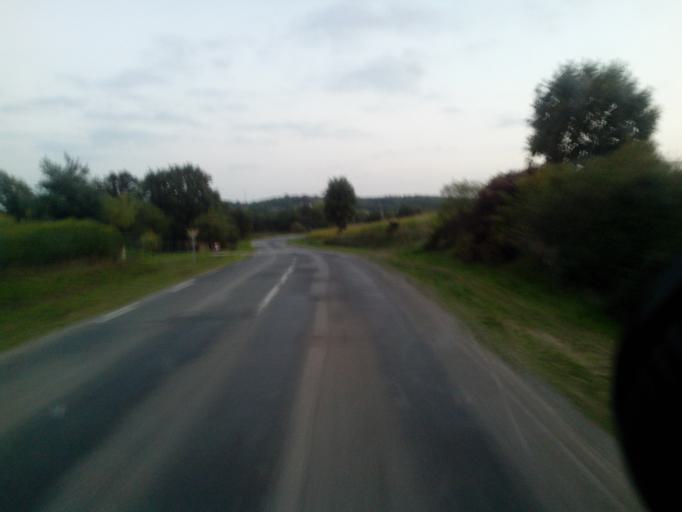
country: FR
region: Brittany
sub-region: Departement d'Ille-et-Vilaine
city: Iffendic
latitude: 48.1243
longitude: -2.0369
